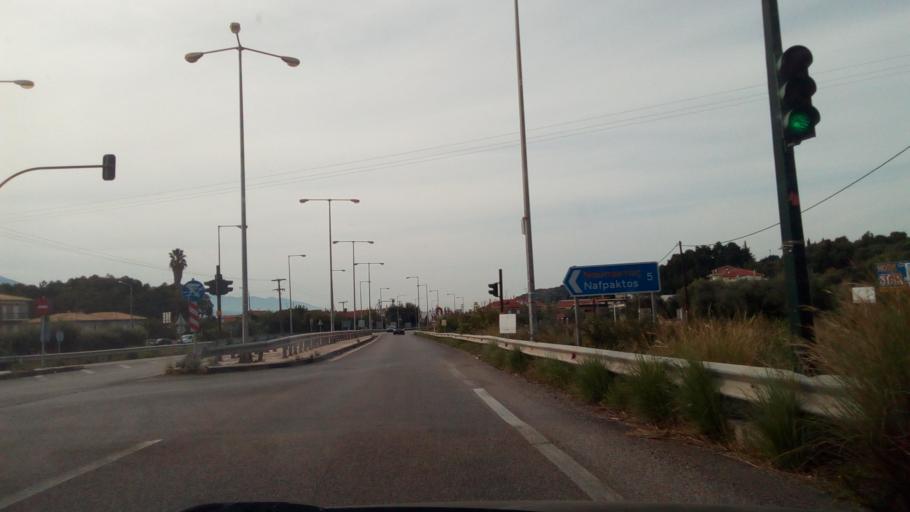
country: GR
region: West Greece
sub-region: Nomos Aitolias kai Akarnanias
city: Antirrio
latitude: 38.3705
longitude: 21.7808
